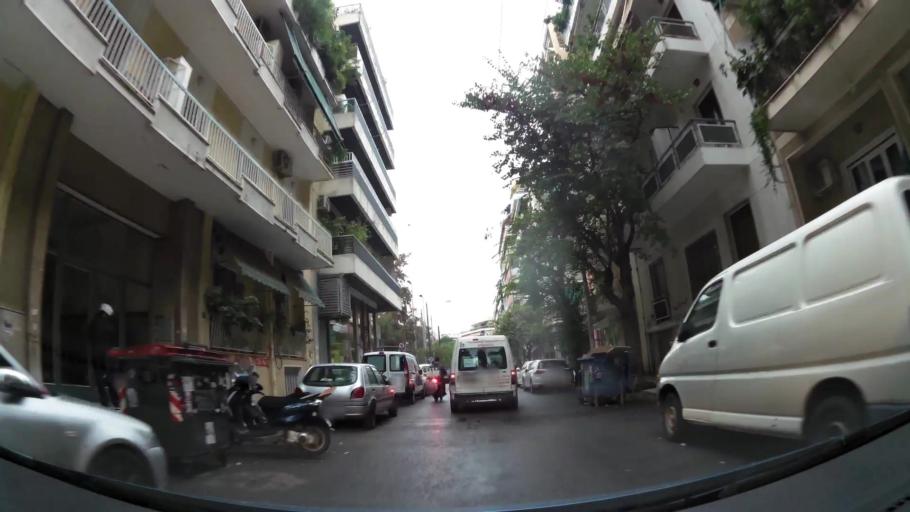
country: GR
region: Attica
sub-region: Nomarchia Athinas
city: Vyronas
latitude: 37.9649
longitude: 23.7479
